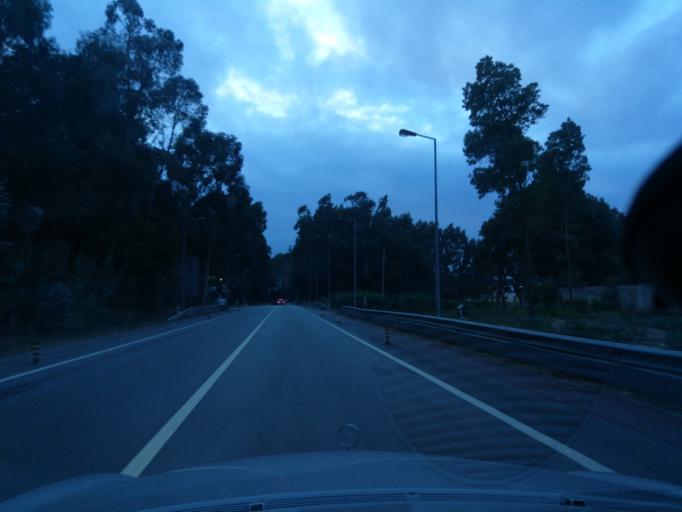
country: PT
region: Aveiro
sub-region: Murtosa
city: Murtosa
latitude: 40.7620
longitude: -8.6356
